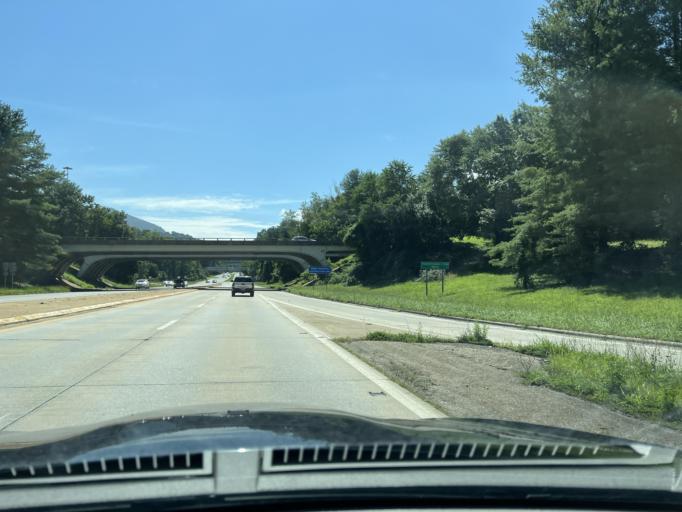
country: US
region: North Carolina
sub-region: Buncombe County
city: Biltmore Forest
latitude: 35.5650
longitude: -82.5001
